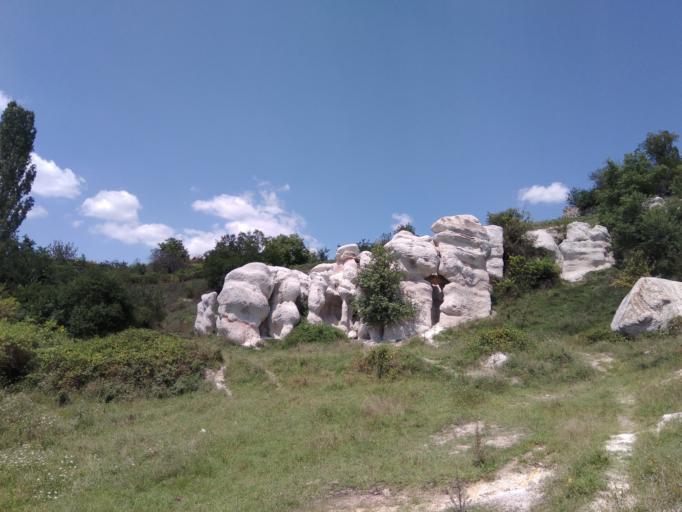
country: BG
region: Kurdzhali
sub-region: Obshtina Kurdzhali
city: Kurdzhali
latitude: 41.6569
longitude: 25.3988
